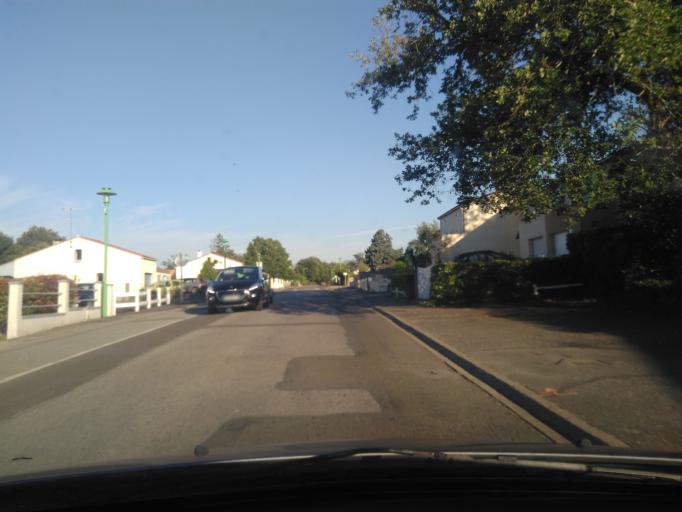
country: FR
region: Pays de la Loire
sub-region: Departement de la Vendee
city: Dompierre-sur-Yon
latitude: 46.7357
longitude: -1.3919
